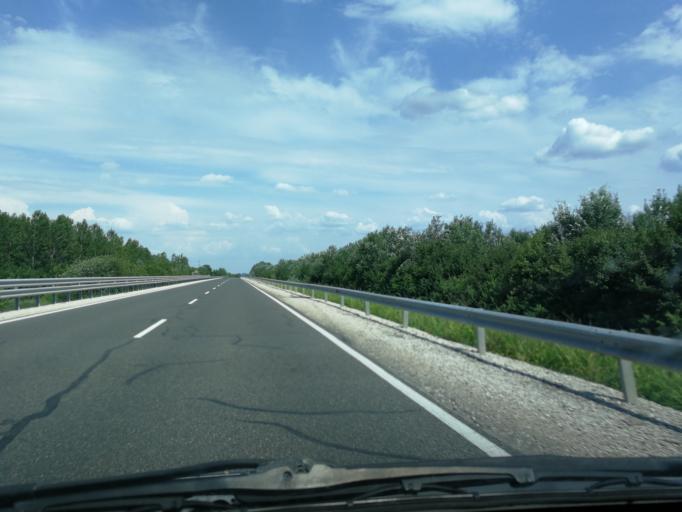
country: HU
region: Tolna
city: Bogyiszlo
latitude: 46.3759
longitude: 18.7843
